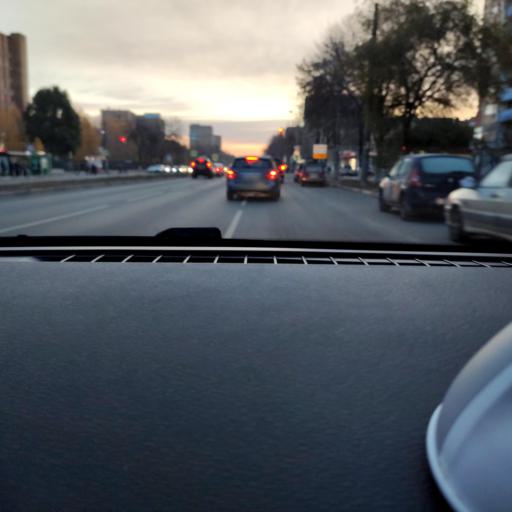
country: RU
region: Samara
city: Samara
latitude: 53.1999
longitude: 50.1667
